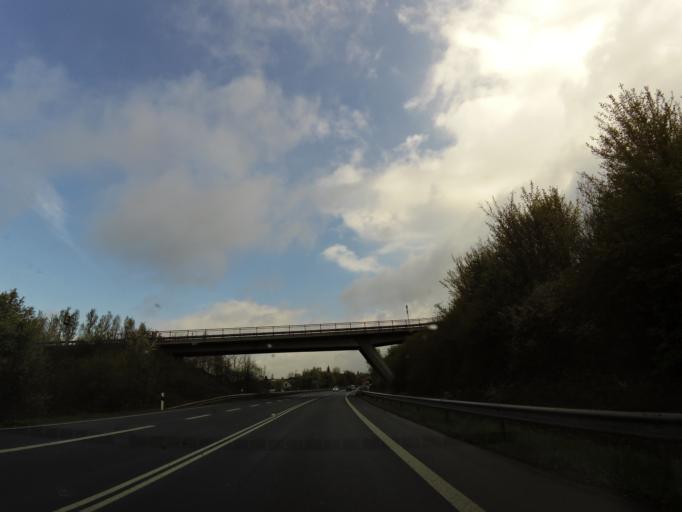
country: DE
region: Lower Saxony
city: Bovenden
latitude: 51.5825
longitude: 9.9233
